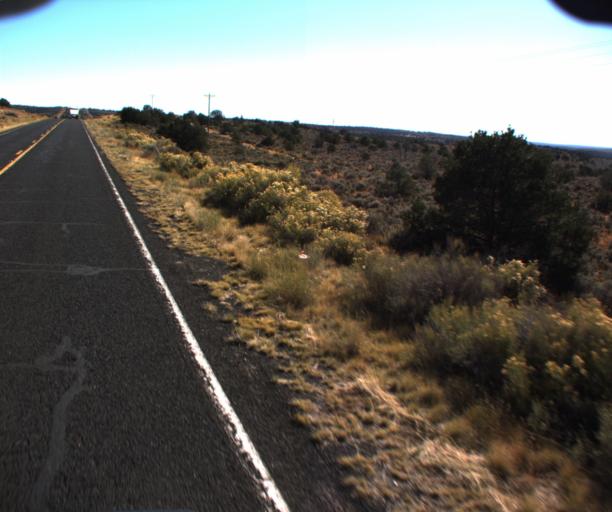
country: US
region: Arizona
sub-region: Apache County
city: Ganado
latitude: 35.6565
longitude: -109.5486
